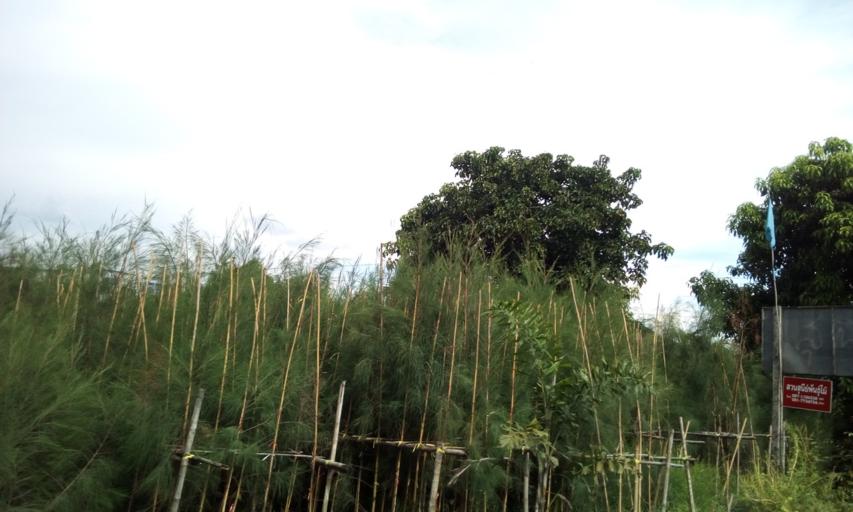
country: TH
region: Nakhon Nayok
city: Ongkharak
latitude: 14.0854
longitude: 100.9145
